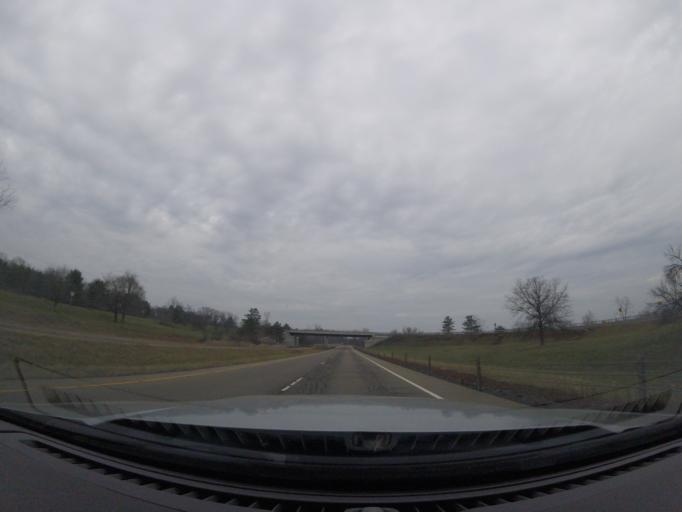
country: US
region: New York
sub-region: Schuyler County
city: Watkins Glen
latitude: 42.4204
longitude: -76.9034
